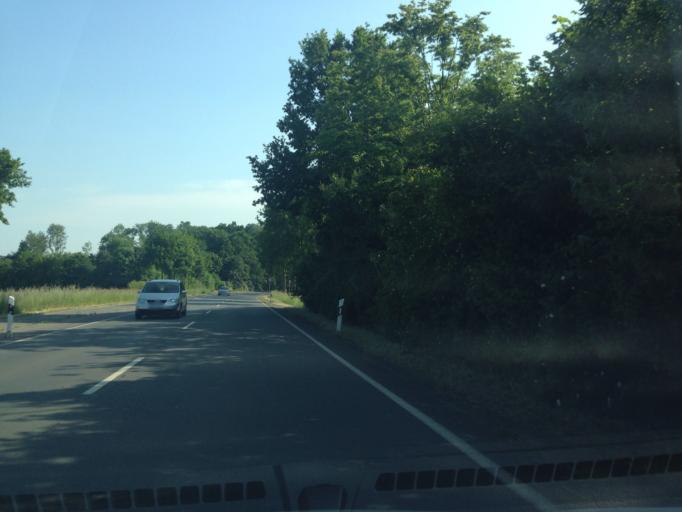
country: DE
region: North Rhine-Westphalia
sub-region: Regierungsbezirk Munster
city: Muenster
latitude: 52.0035
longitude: 7.5573
